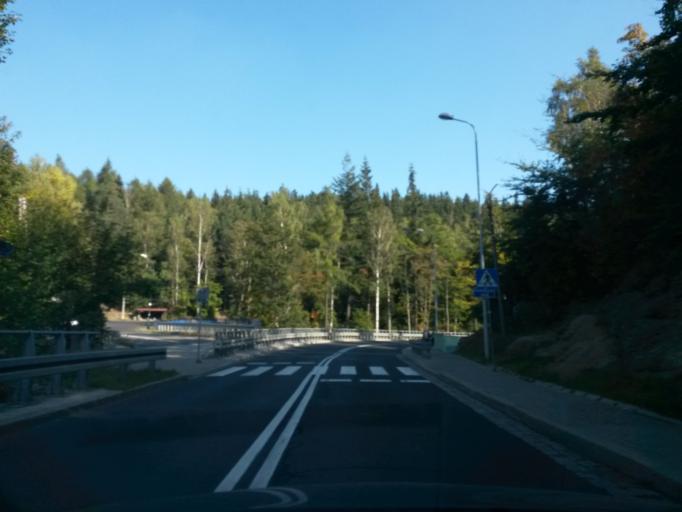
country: PL
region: Lower Silesian Voivodeship
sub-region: Powiat jeleniogorski
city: Szklarska Poreba
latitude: 50.8261
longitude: 15.5074
